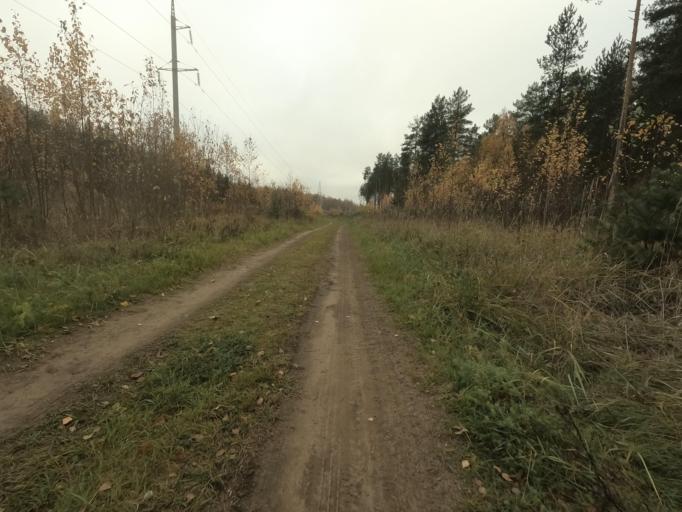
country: RU
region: Leningrad
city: Kirovsk
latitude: 59.8501
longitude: 30.9833
